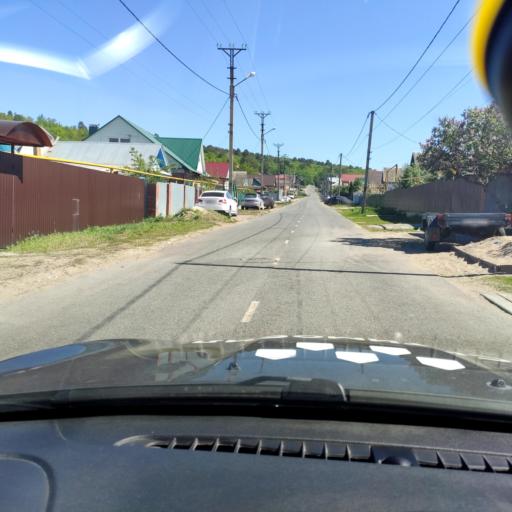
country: RU
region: Samara
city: Zhigulevsk
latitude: 53.4683
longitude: 49.6430
